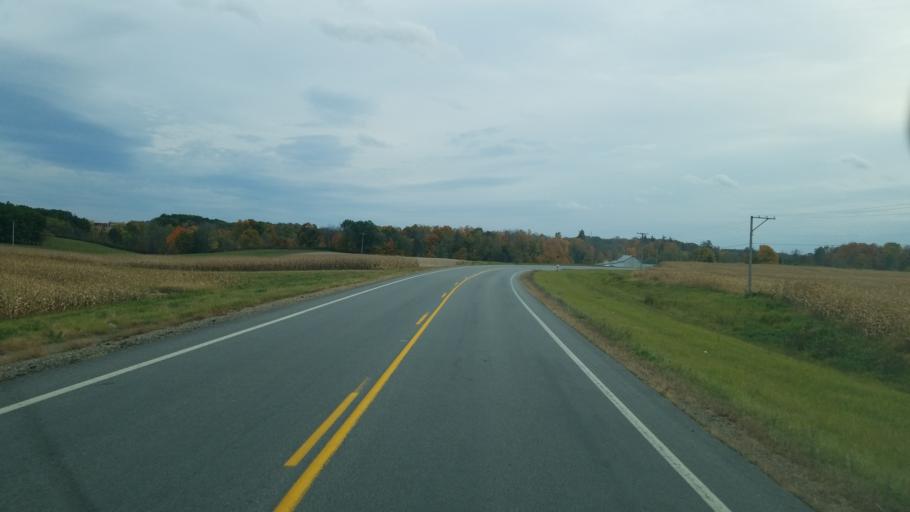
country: US
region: Ohio
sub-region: Ashland County
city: Ashland
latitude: 40.8180
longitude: -82.2992
